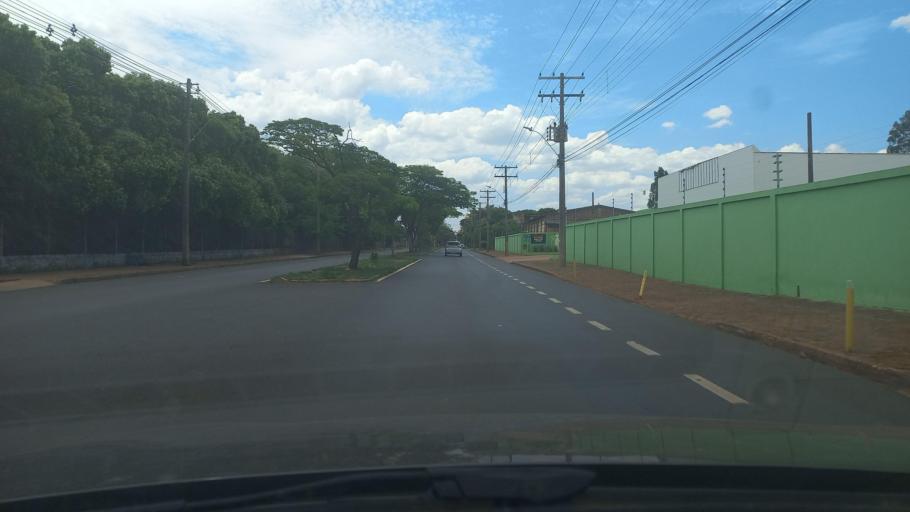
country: BR
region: Minas Gerais
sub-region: Uberaba
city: Uberaba
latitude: -19.7464
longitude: -47.9778
